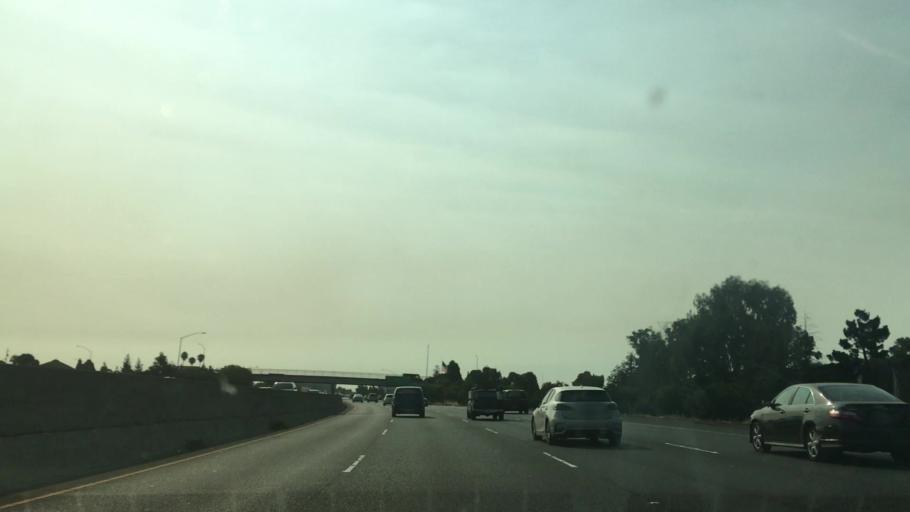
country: US
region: California
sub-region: San Mateo County
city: Redwood City
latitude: 37.4985
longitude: -122.2371
